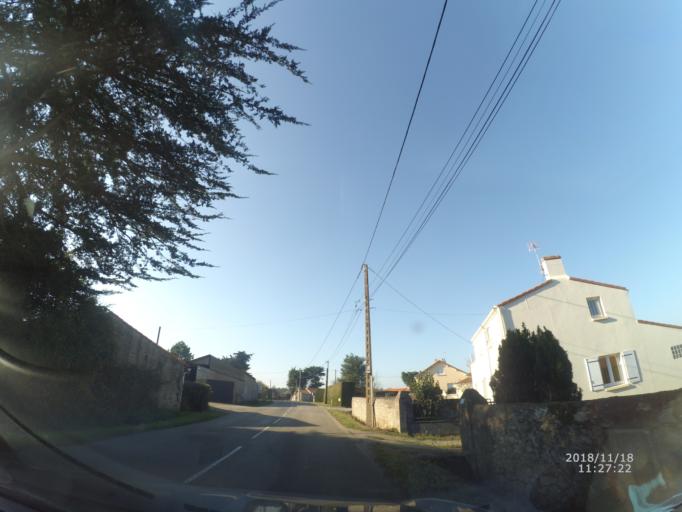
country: FR
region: Pays de la Loire
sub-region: Departement de la Loire-Atlantique
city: Saint-Brevin-les-Pins
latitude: 47.2199
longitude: -2.1413
